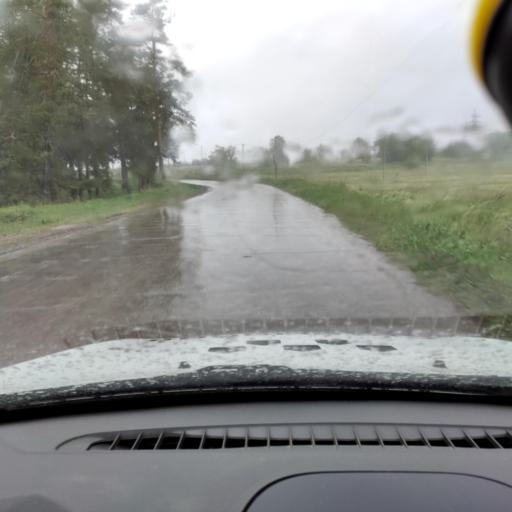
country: RU
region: Samara
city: Zhigulevsk
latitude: 53.5548
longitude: 49.5440
